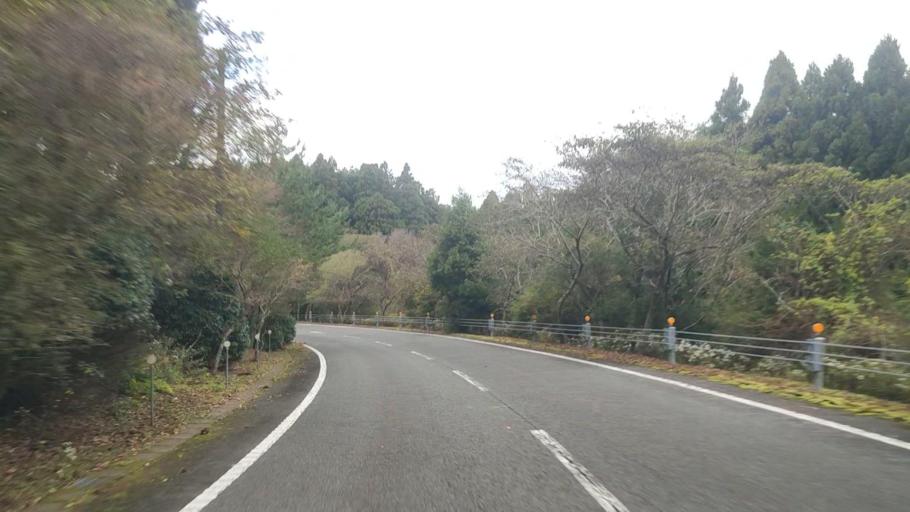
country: JP
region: Shizuoka
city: Heda
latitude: 34.9149
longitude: 138.8464
